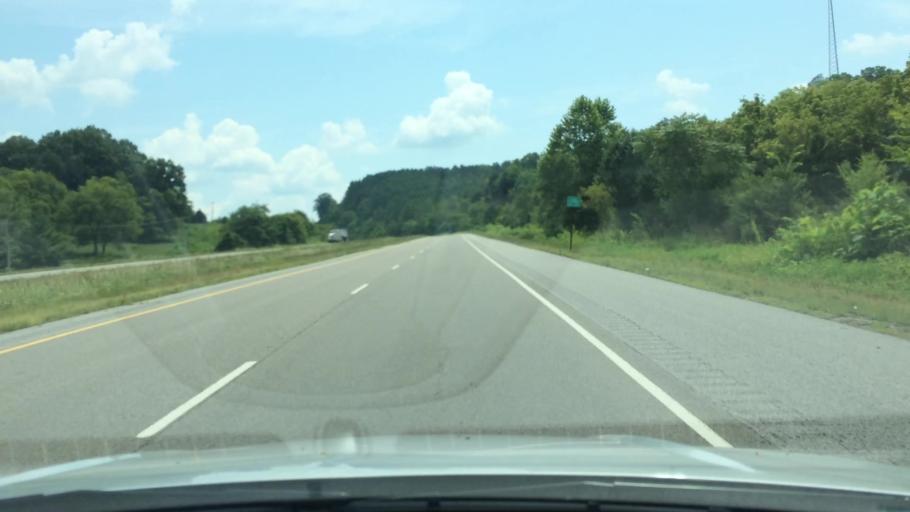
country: US
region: Tennessee
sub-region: Giles County
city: Pulaski
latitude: 35.1753
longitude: -86.9952
